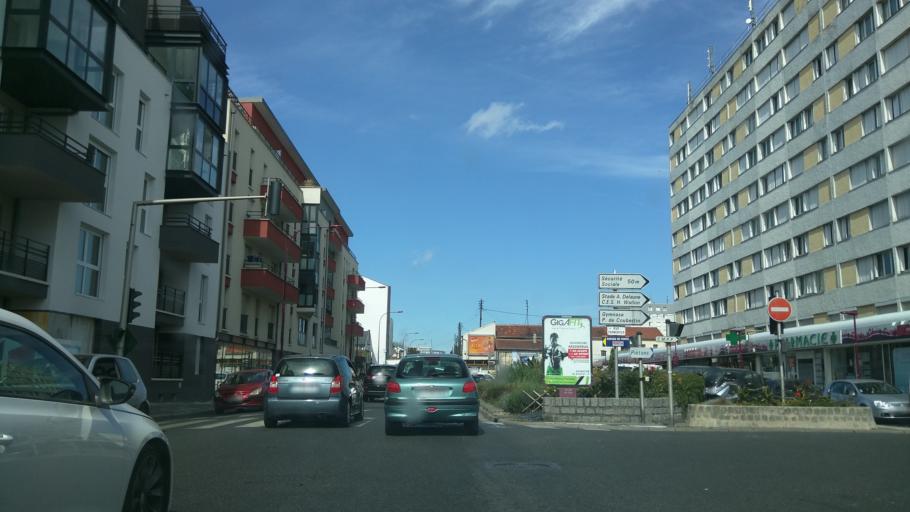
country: FR
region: Ile-de-France
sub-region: Departement du Val-d'Oise
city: Bezons
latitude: 48.9288
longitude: 2.2144
